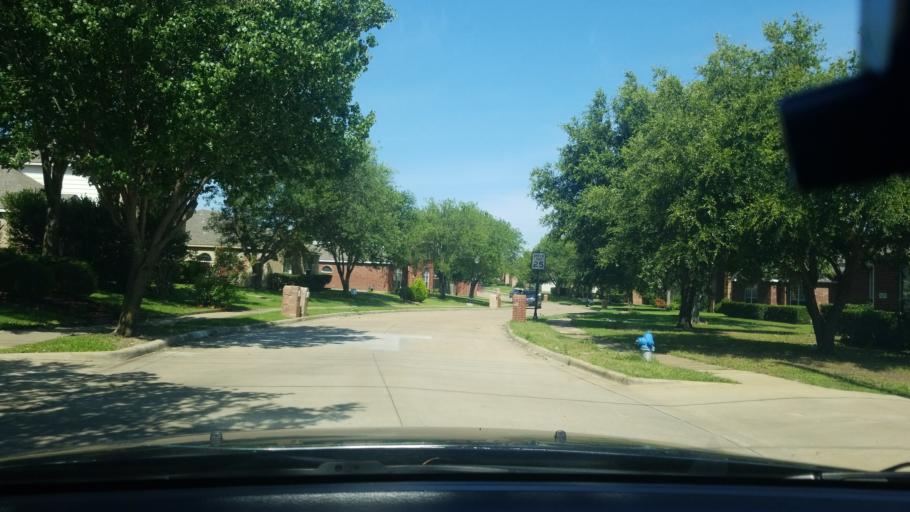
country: US
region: Texas
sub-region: Dallas County
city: Mesquite
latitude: 32.7739
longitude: -96.5856
